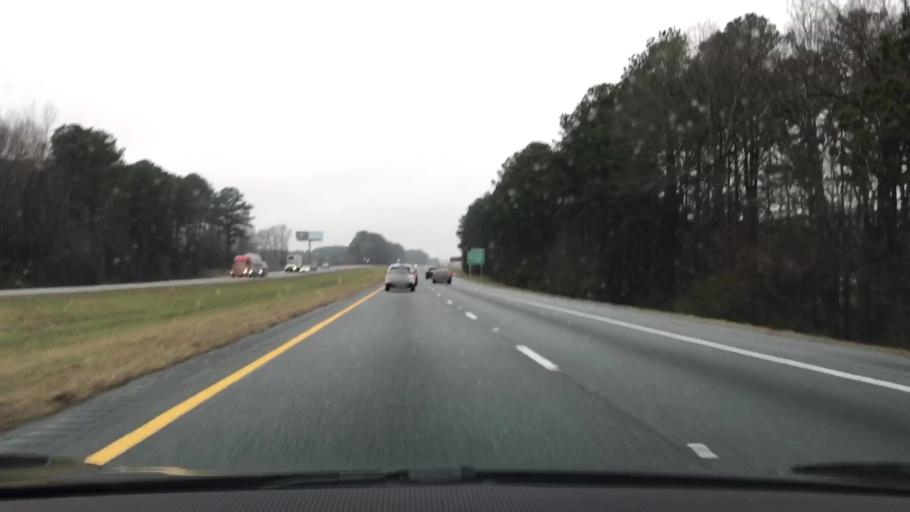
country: US
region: Georgia
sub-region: Walton County
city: Social Circle
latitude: 33.5886
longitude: -83.6161
